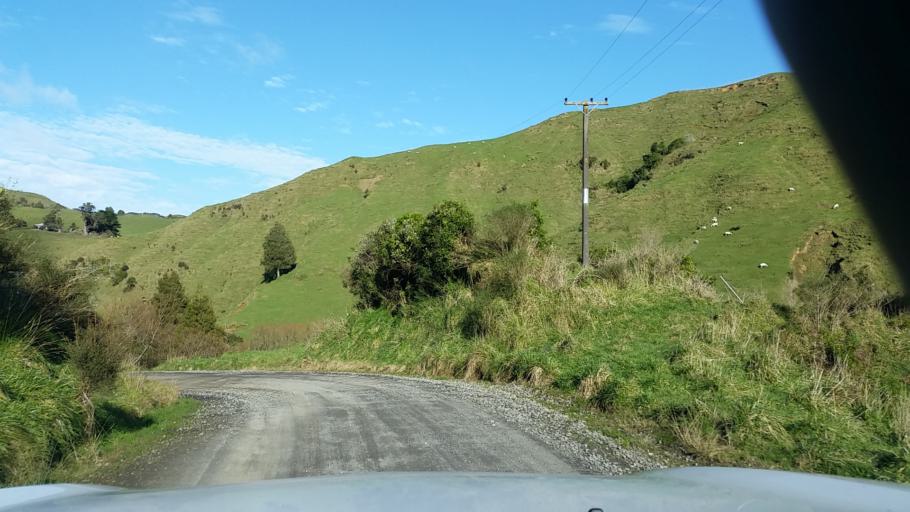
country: NZ
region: Taranaki
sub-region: South Taranaki District
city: Eltham
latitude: -39.5069
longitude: 174.3975
